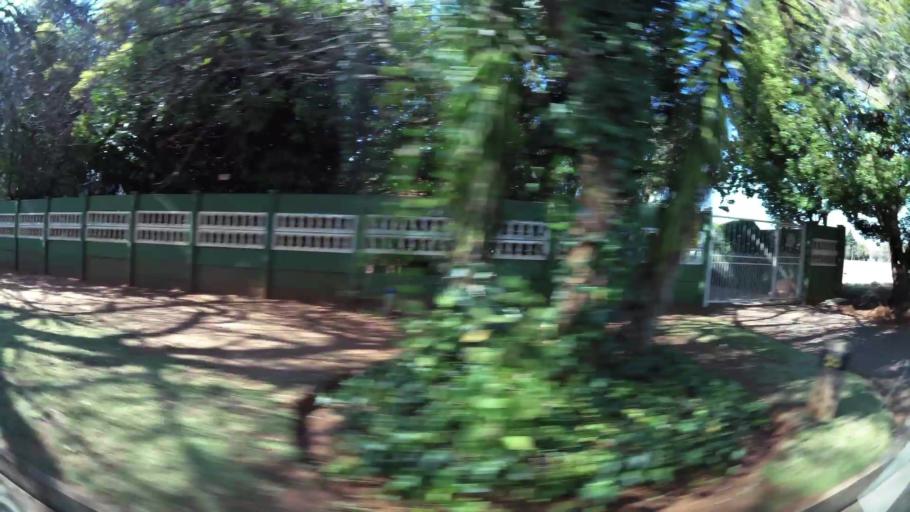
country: ZA
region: Gauteng
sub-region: Ekurhuleni Metropolitan Municipality
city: Benoni
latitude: -26.1410
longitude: 28.3396
